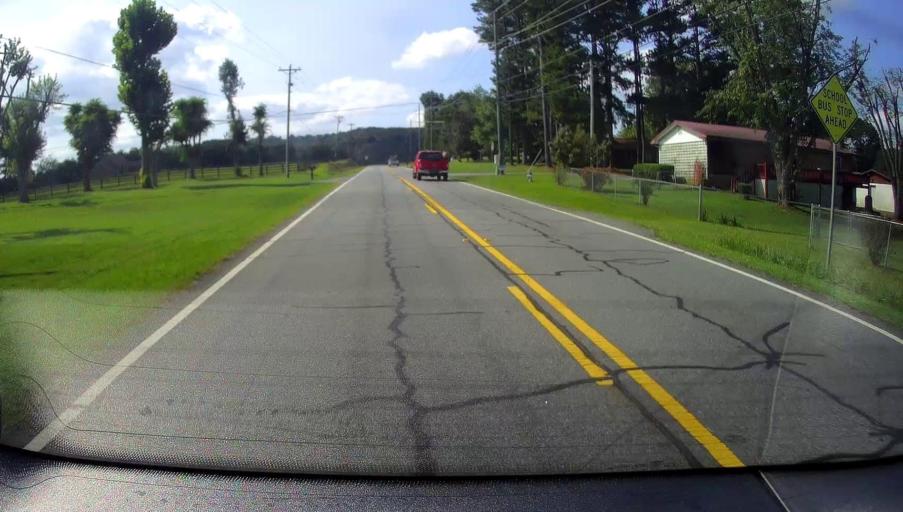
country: US
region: Georgia
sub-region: Catoosa County
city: Ringgold
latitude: 34.9090
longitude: -85.0821
